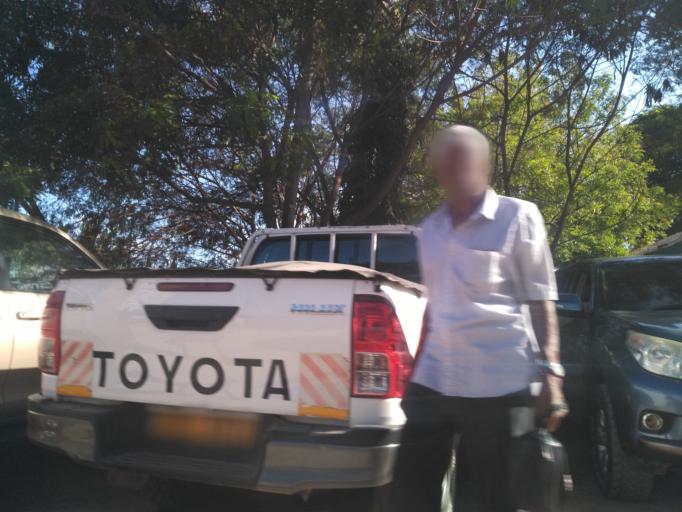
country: TZ
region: Dar es Salaam
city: Magomeni
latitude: -6.7781
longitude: 39.2650
